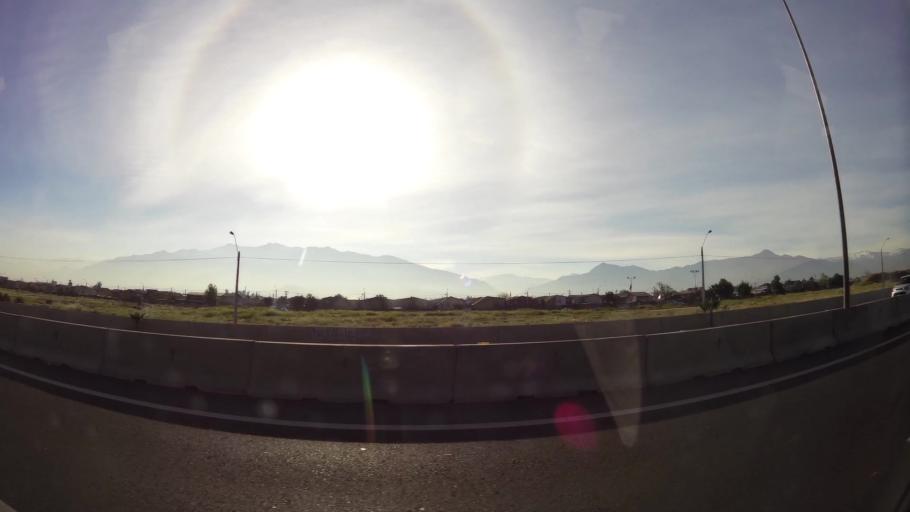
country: CL
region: Santiago Metropolitan
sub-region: Provincia de Santiago
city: La Pintana
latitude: -33.5731
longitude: -70.6123
